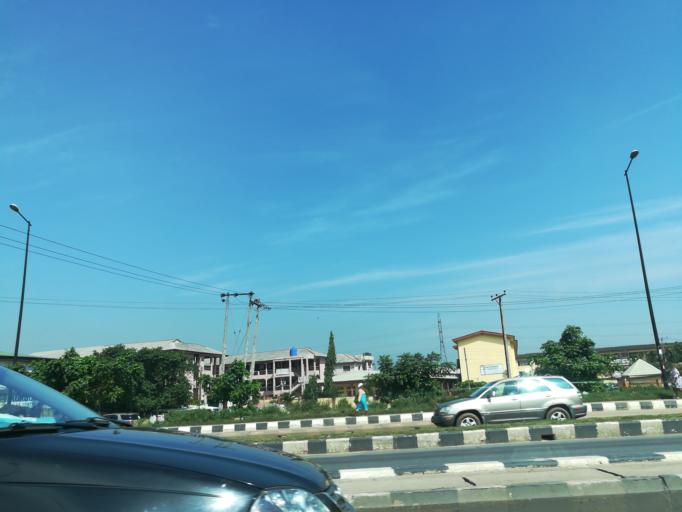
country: NG
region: Lagos
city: Ebute Ikorodu
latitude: 6.6217
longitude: 3.4815
